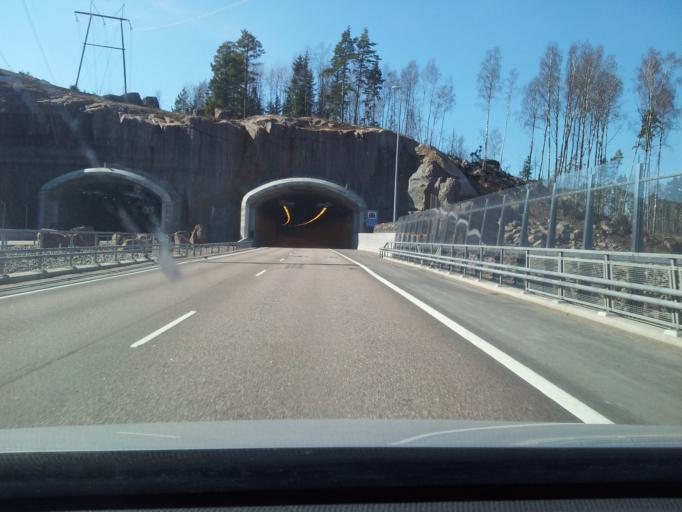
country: FI
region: Uusimaa
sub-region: Loviisa
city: Ruotsinpyhtaeae
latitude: 60.4926
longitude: 26.4463
